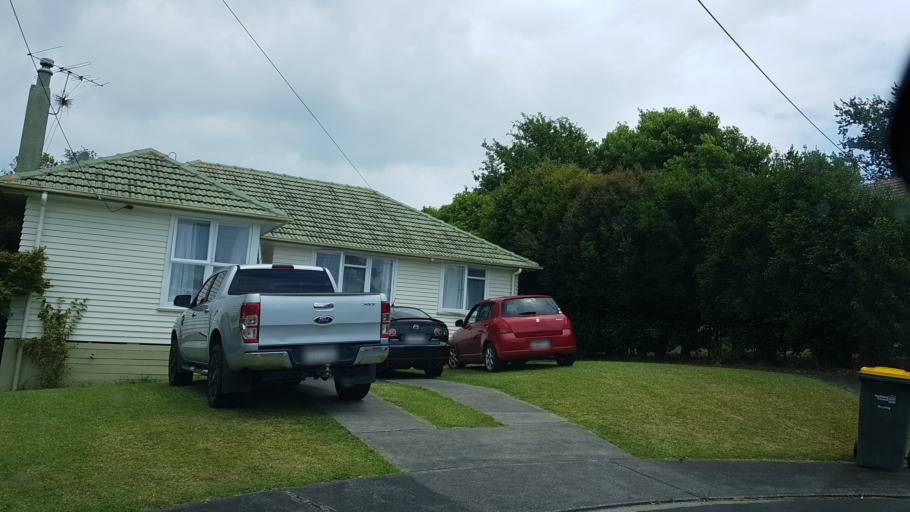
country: NZ
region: Auckland
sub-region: Auckland
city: North Shore
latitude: -36.8021
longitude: 174.7790
